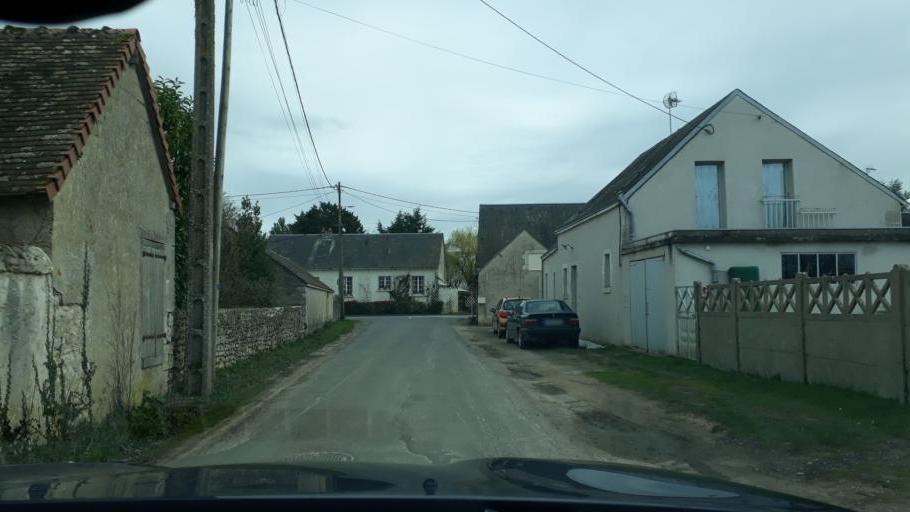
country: FR
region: Centre
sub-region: Departement du Loir-et-Cher
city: Mer
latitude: 47.7691
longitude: 1.4410
